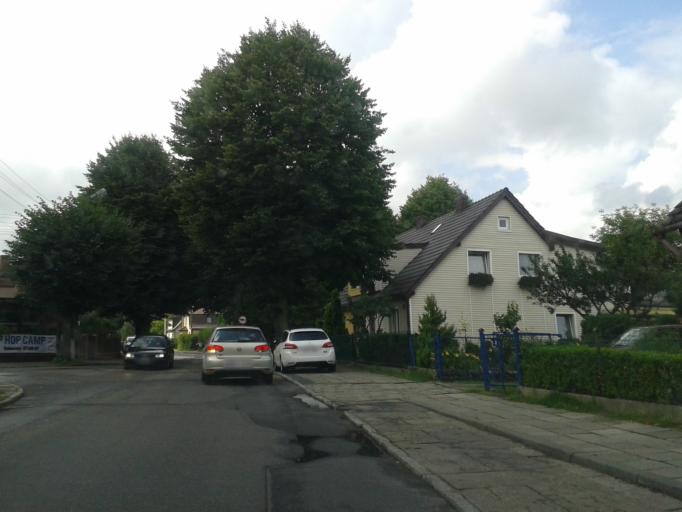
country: PL
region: West Pomeranian Voivodeship
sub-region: Swinoujscie
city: Swinoujscie
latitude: 53.9072
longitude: 14.2312
